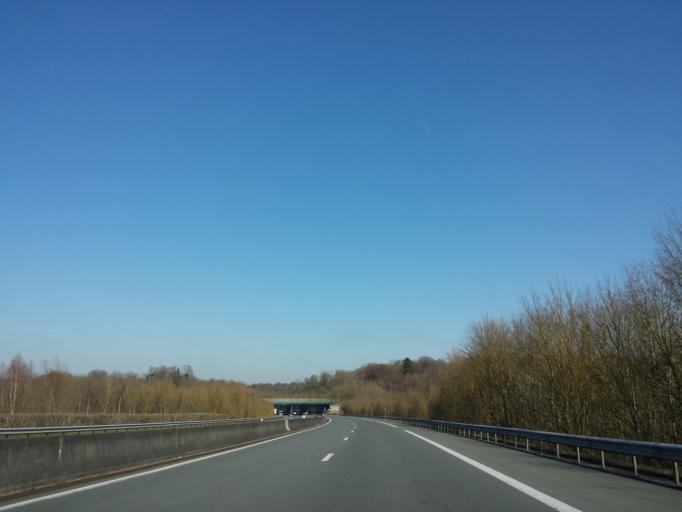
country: FR
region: Picardie
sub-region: Departement de la Somme
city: Saleux
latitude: 49.8303
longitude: 2.2536
